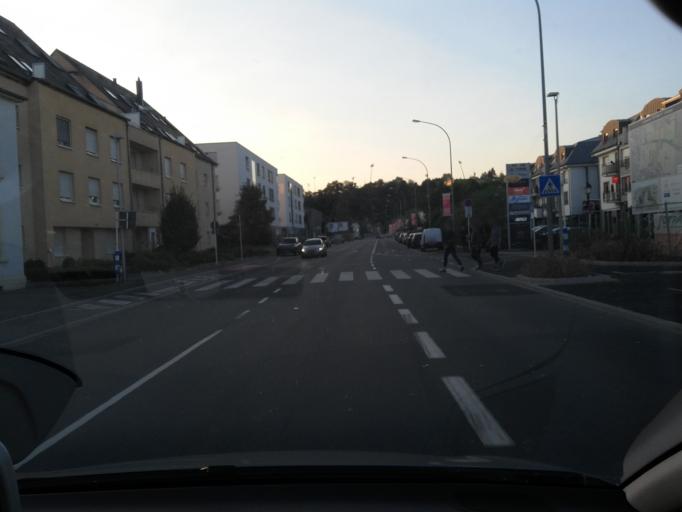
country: LU
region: Luxembourg
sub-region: Canton de Luxembourg
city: Alzingen
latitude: 49.5700
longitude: 6.1608
